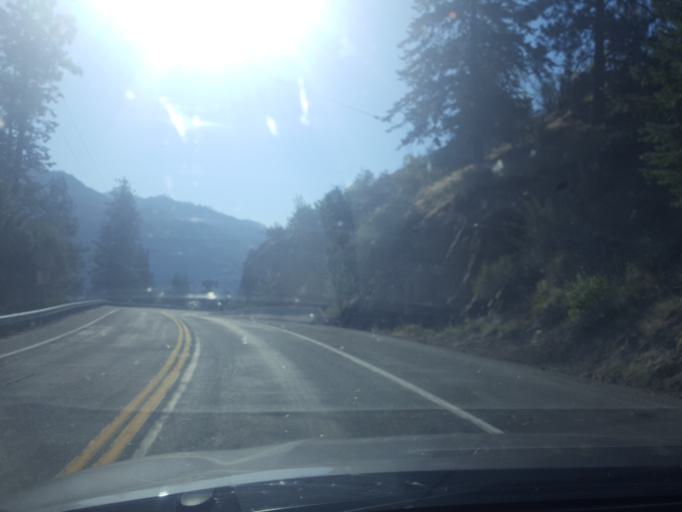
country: US
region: Washington
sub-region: Chelan County
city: Granite Falls
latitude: 47.9888
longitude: -120.2430
